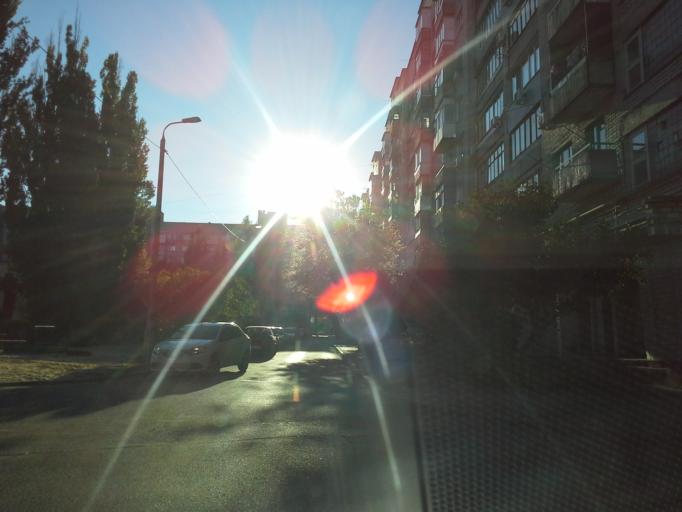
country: RU
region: Volgograd
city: Vodstroy
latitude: 48.8216
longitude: 44.6387
